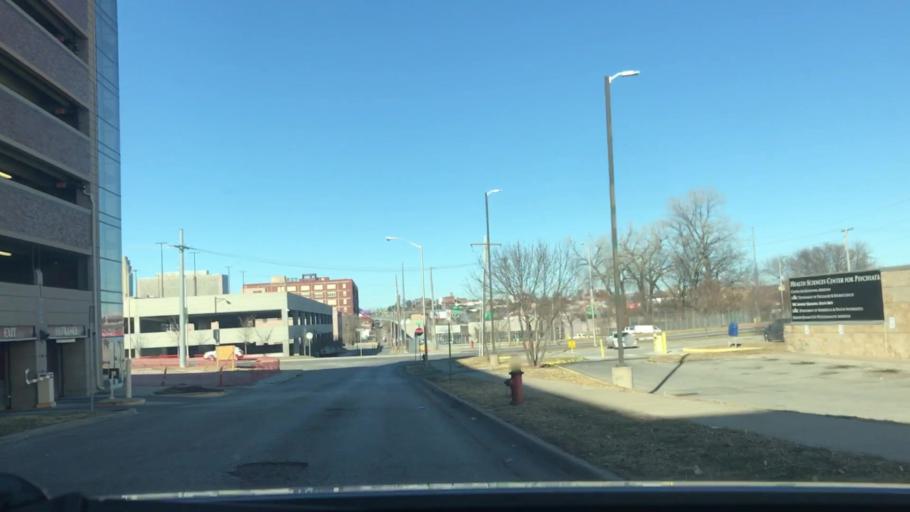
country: US
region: Missouri
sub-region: Jackson County
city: Kansas City
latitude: 39.0855
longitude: -94.5732
